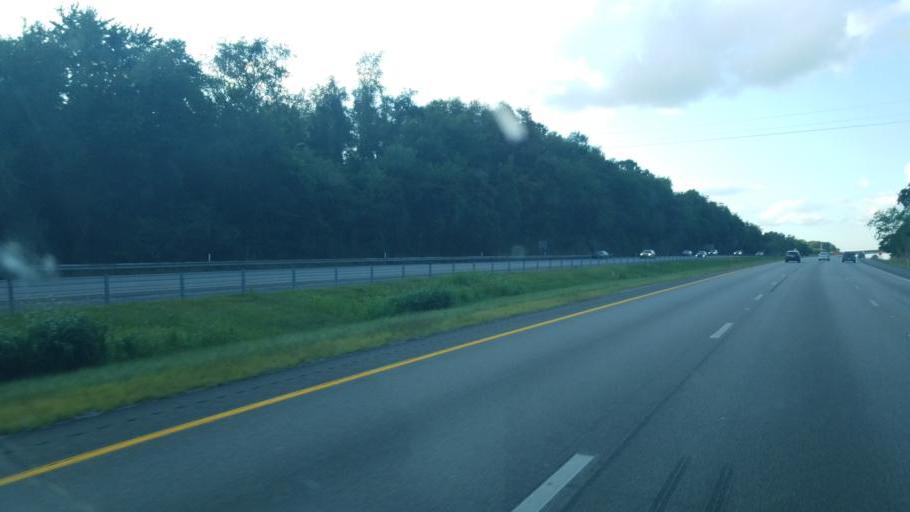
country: US
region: Pennsylvania
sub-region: Allegheny County
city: Bradford Woods
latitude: 40.6364
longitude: -80.0978
